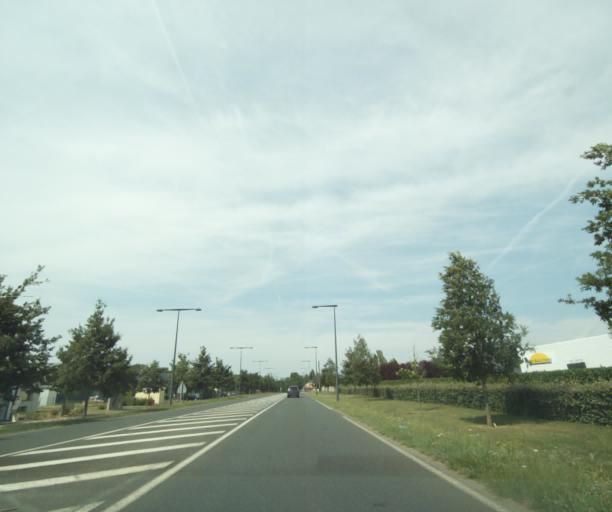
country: FR
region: Centre
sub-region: Departement d'Indre-et-Loire
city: Montbazon
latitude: 47.2768
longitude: 0.7099
